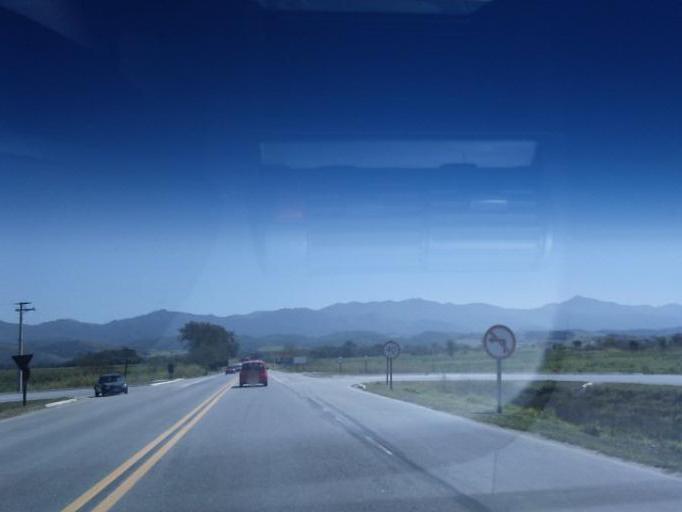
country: BR
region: Sao Paulo
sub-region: Taubate
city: Taubate
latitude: -22.9963
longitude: -45.6426
